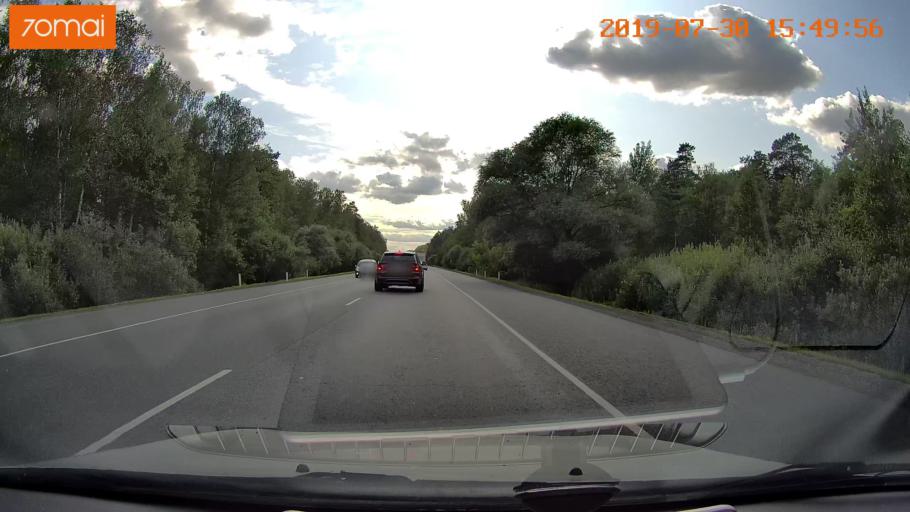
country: RU
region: Moskovskaya
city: Voskresensk
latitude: 55.3347
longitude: 38.6592
